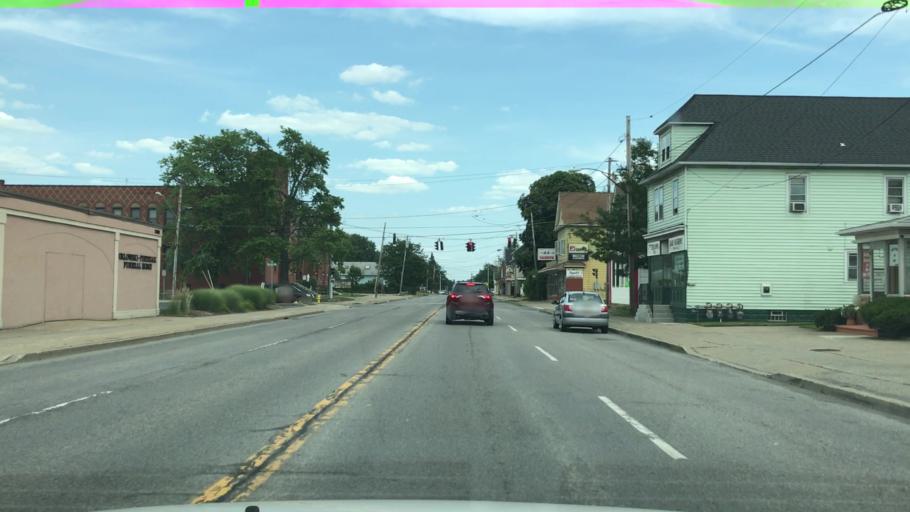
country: US
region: New York
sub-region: Erie County
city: Sloan
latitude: 42.8843
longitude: -78.7822
